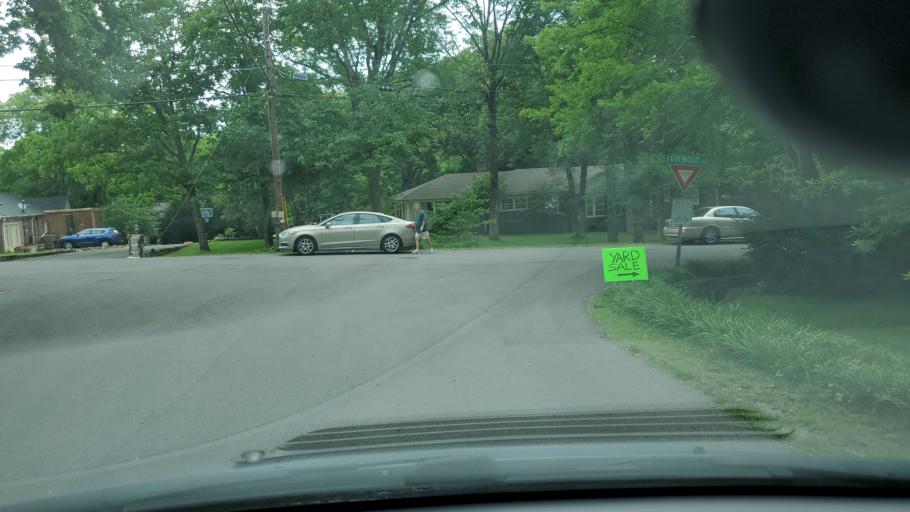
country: US
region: Tennessee
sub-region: Davidson County
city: Lakewood
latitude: 36.2288
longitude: -86.7180
